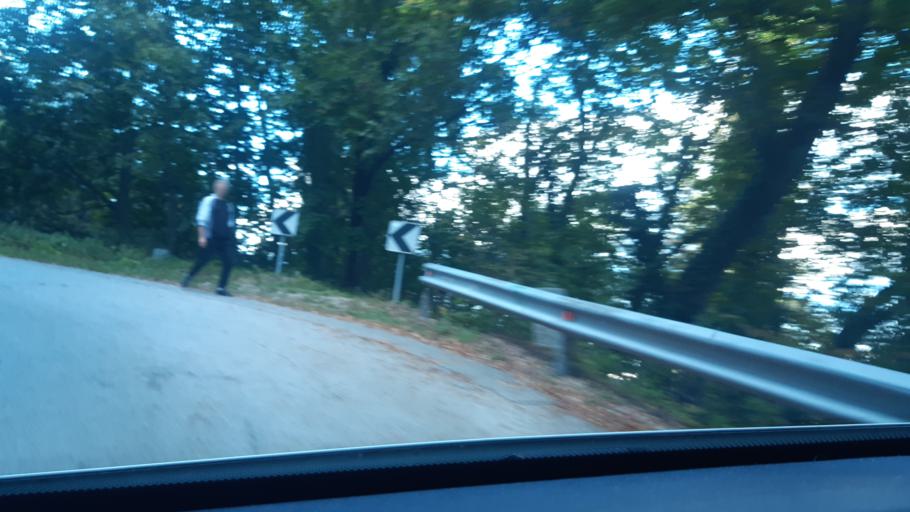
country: SI
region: Kranj
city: Kranj
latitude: 46.2433
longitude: 14.3382
